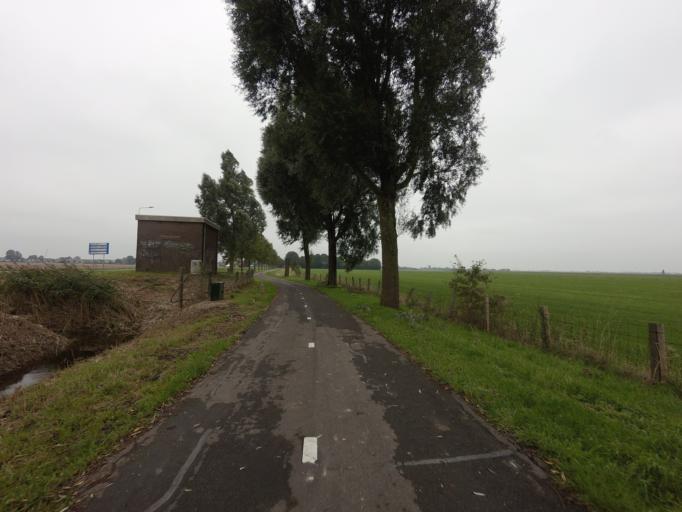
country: NL
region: South Holland
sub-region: Gemeente Nieuwkoop
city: Nieuwkoop
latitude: 52.1767
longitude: 4.7702
